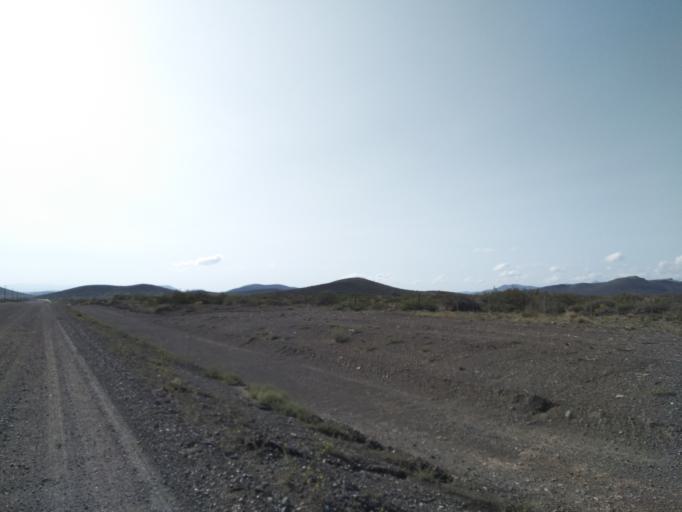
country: AR
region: Mendoza
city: Malargue
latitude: -35.6591
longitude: -69.5452
